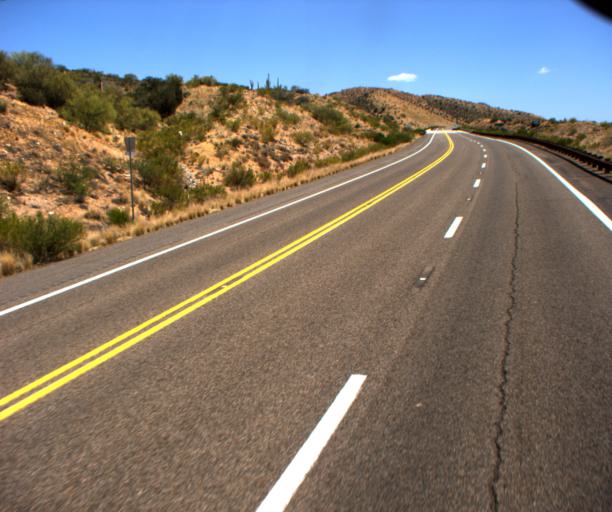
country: US
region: Arizona
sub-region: Gila County
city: Miami
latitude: 33.5633
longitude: -110.9531
